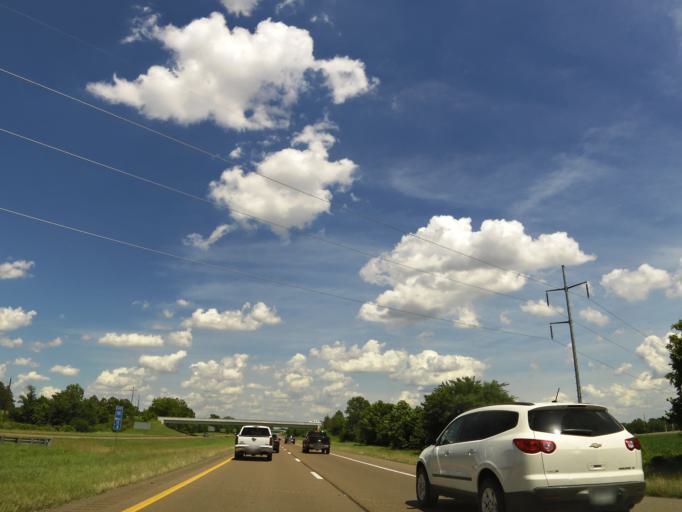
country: US
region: Tennessee
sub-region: Dyer County
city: Dyersburg
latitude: 36.0684
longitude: -89.3816
